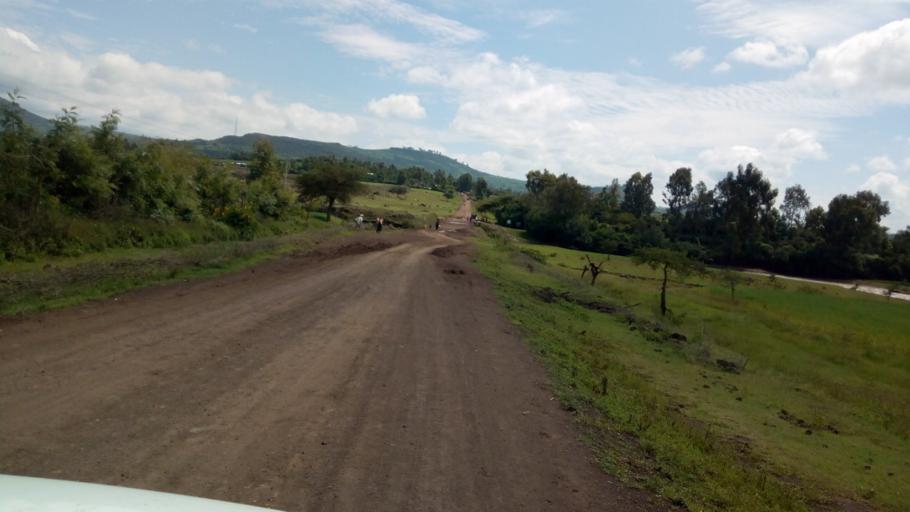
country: ET
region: Oromiya
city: Bishoftu
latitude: 8.8411
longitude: 39.0134
